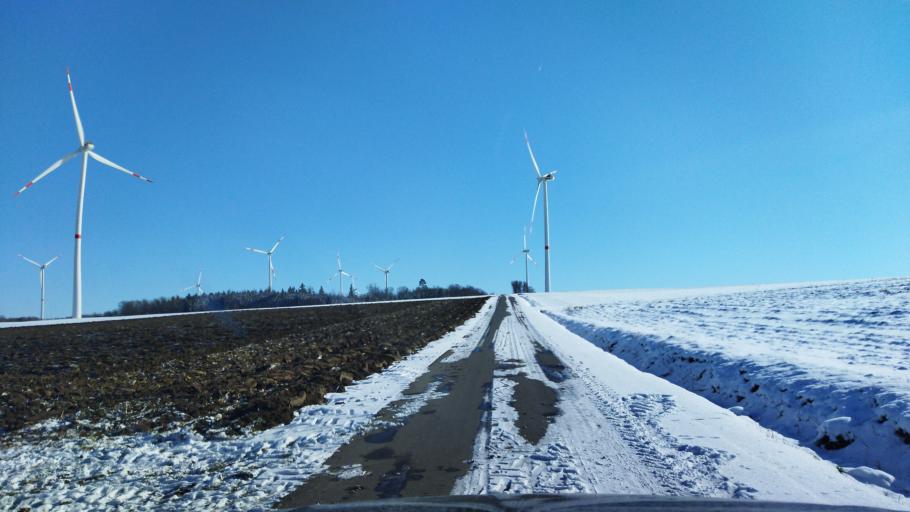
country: DE
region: Baden-Wuerttemberg
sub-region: Regierungsbezirk Stuttgart
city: Ilshofen
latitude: 49.1919
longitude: 9.9411
